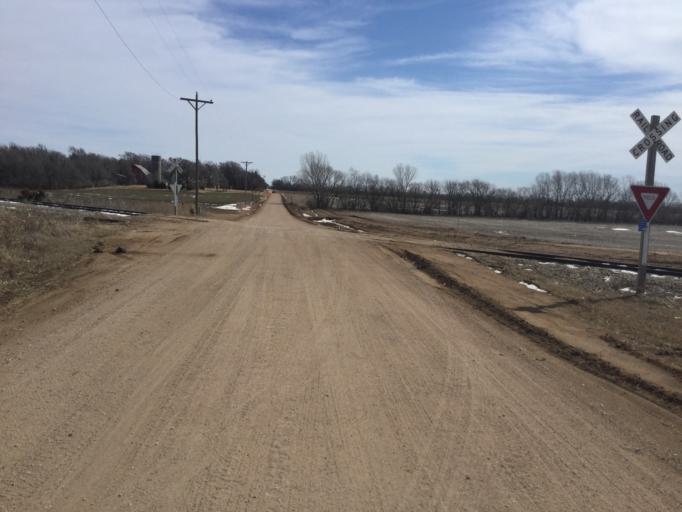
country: US
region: Kansas
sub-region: Sedgwick County
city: Clearwater
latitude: 37.5191
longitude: -97.4919
